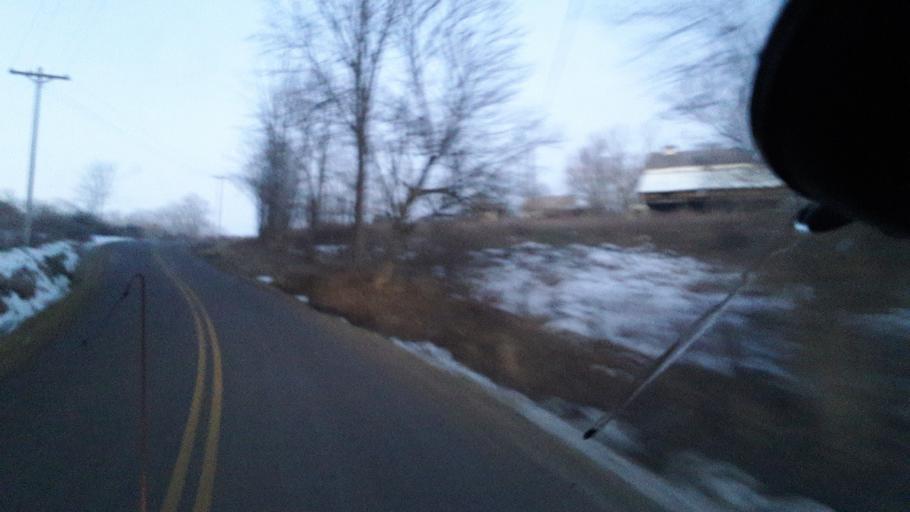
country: US
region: Ohio
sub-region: Perry County
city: New Lexington
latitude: 39.7066
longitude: -82.2785
